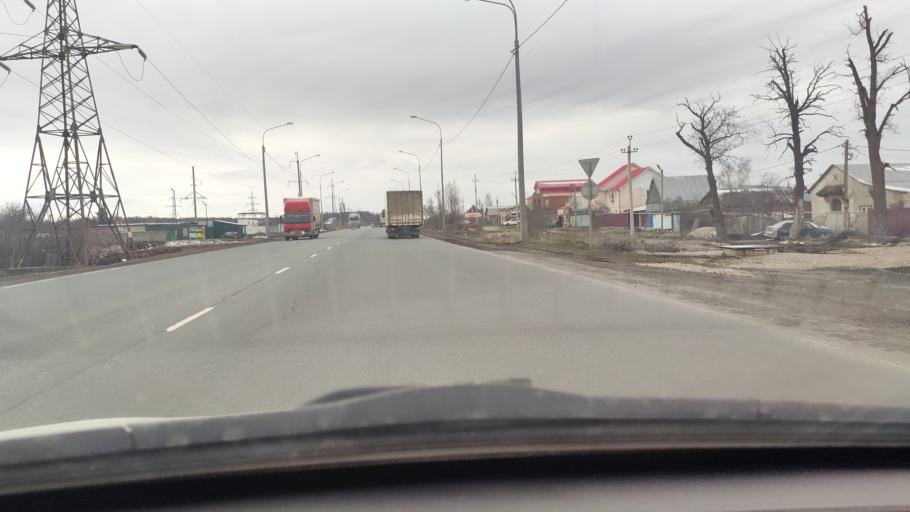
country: RU
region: Samara
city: Zhigulevsk
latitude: 53.3781
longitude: 49.4563
